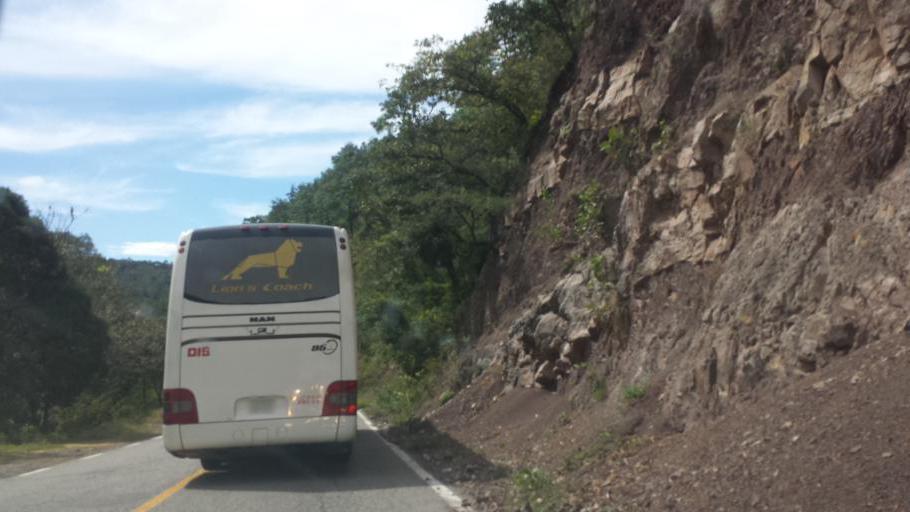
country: MX
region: Oaxaca
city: San Francisco Sola
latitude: 16.4422
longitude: -97.0327
